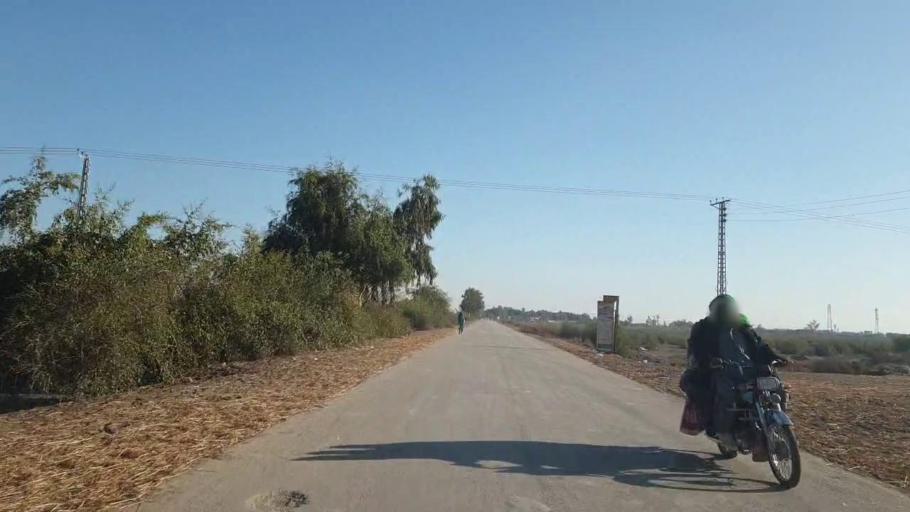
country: PK
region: Sindh
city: Dokri
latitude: 27.3376
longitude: 68.1271
